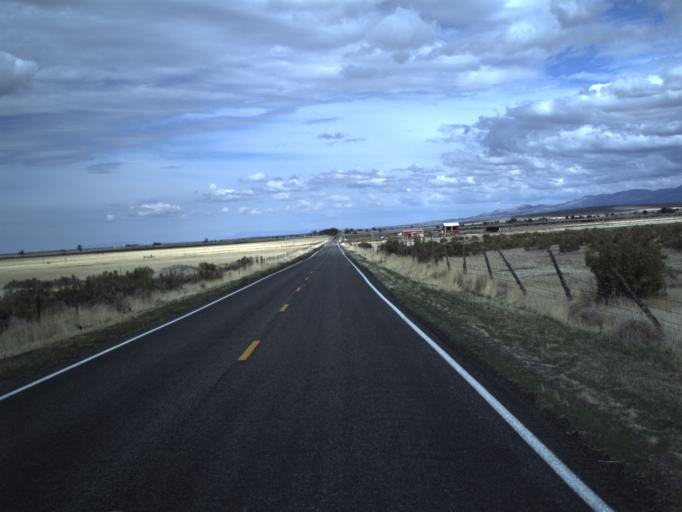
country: US
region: Utah
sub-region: Millard County
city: Fillmore
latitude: 39.0187
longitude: -112.4100
